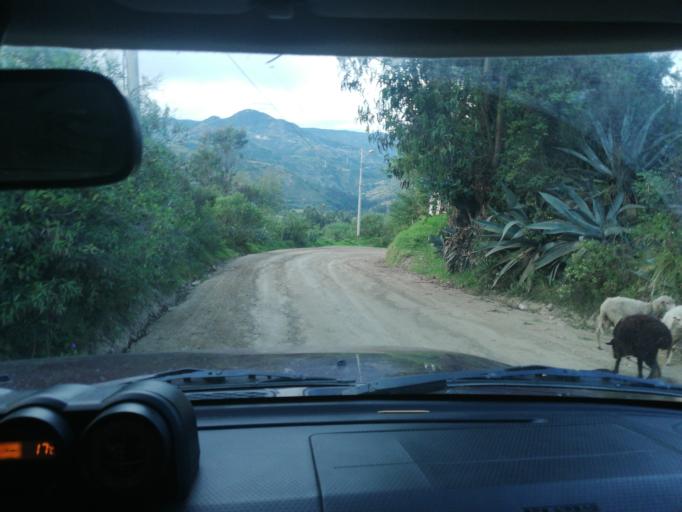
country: EC
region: Azuay
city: Nulti
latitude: -3.0342
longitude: -78.8007
